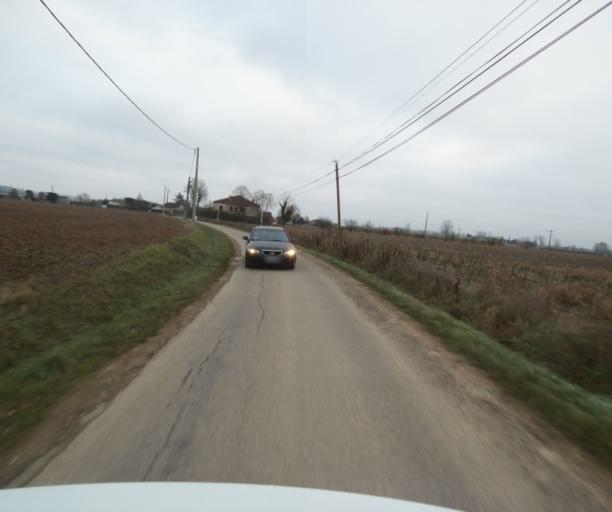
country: FR
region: Midi-Pyrenees
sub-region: Departement du Tarn-et-Garonne
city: Moissac
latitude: 44.1036
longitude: 1.1292
